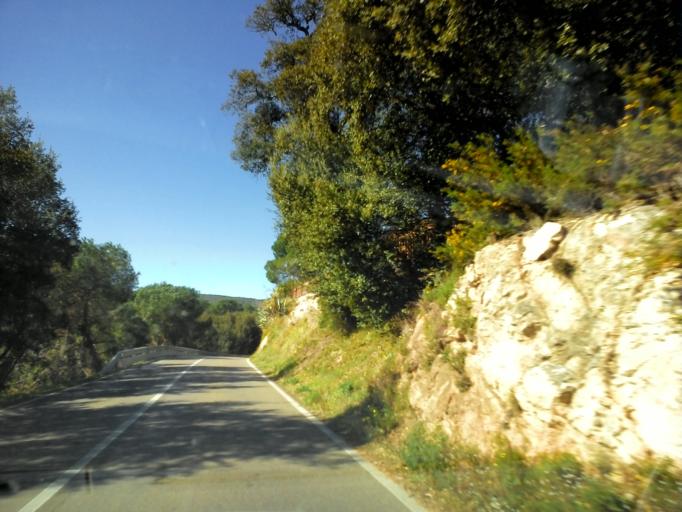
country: ES
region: Catalonia
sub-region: Provincia de Girona
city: Calonge
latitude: 41.8582
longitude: 3.0697
